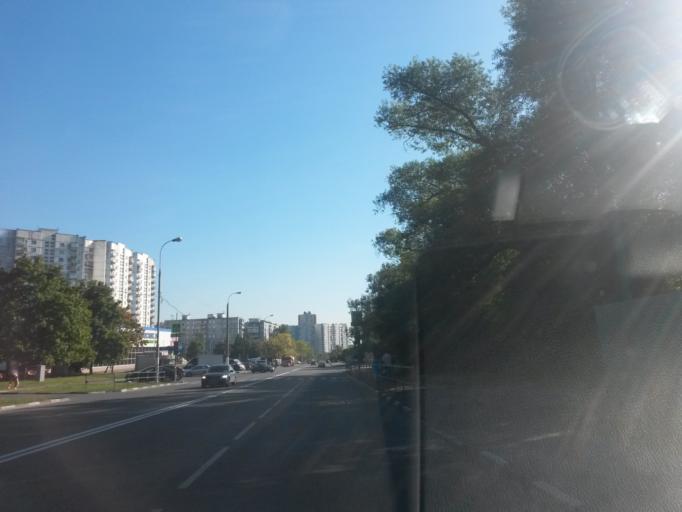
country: RU
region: Moscow
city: Yasenevo
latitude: 55.6082
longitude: 37.5128
